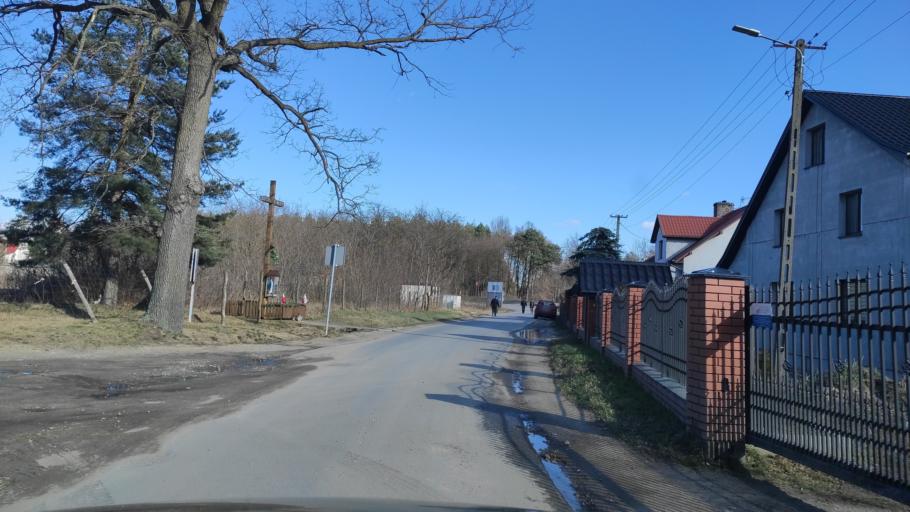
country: PL
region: Masovian Voivodeship
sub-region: Powiat radomski
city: Jedlnia-Letnisko
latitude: 51.4393
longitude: 21.3072
